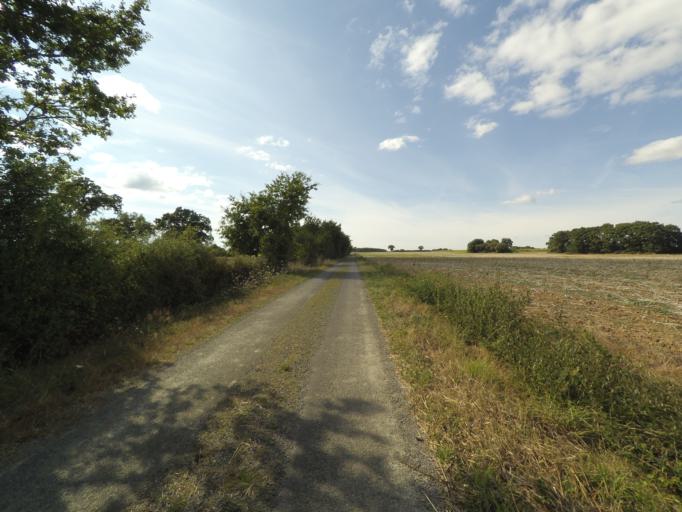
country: FR
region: Pays de la Loire
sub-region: Departement de la Loire-Atlantique
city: Vieillevigne
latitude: 46.9554
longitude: -1.4408
